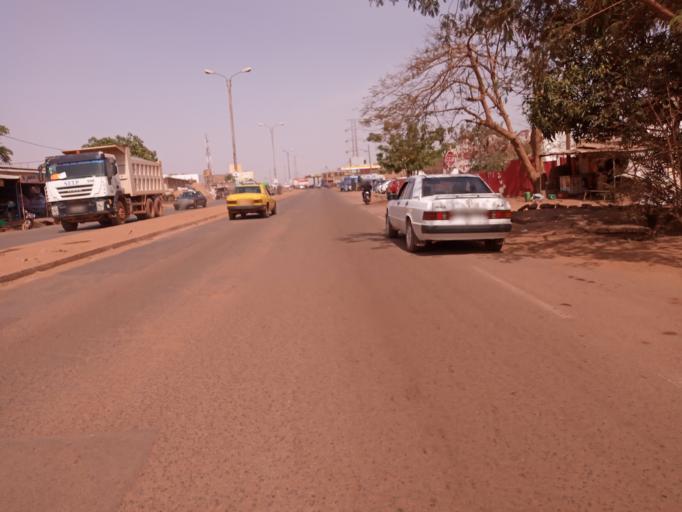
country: ML
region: Bamako
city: Bamako
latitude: 12.5765
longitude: -7.9520
